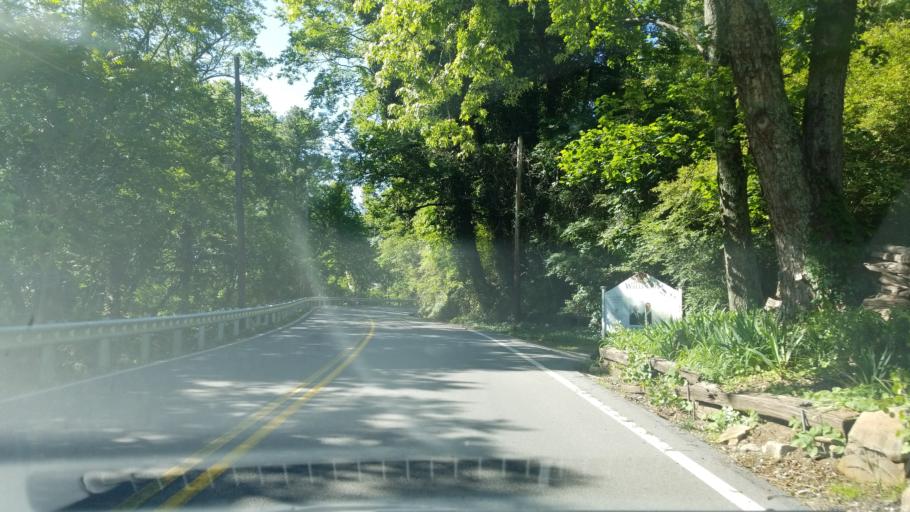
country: US
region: Tennessee
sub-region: Hamilton County
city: Lookout Mountain
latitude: 35.0141
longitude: -85.3373
